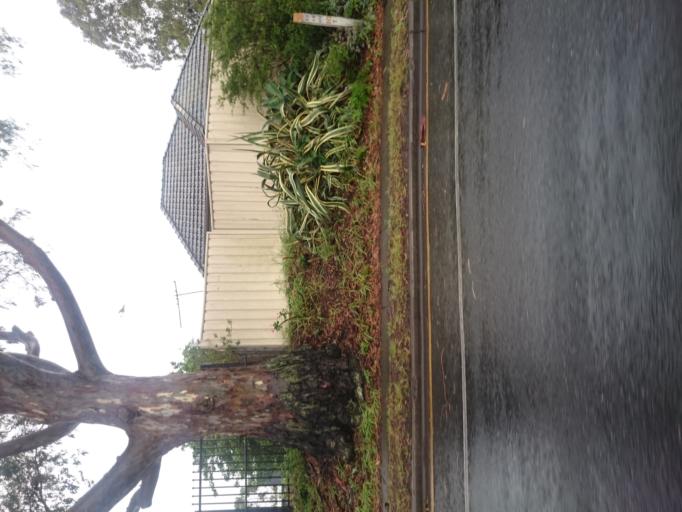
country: AU
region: Queensland
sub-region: Brisbane
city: Cannon Hill
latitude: -27.4733
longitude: 153.1152
